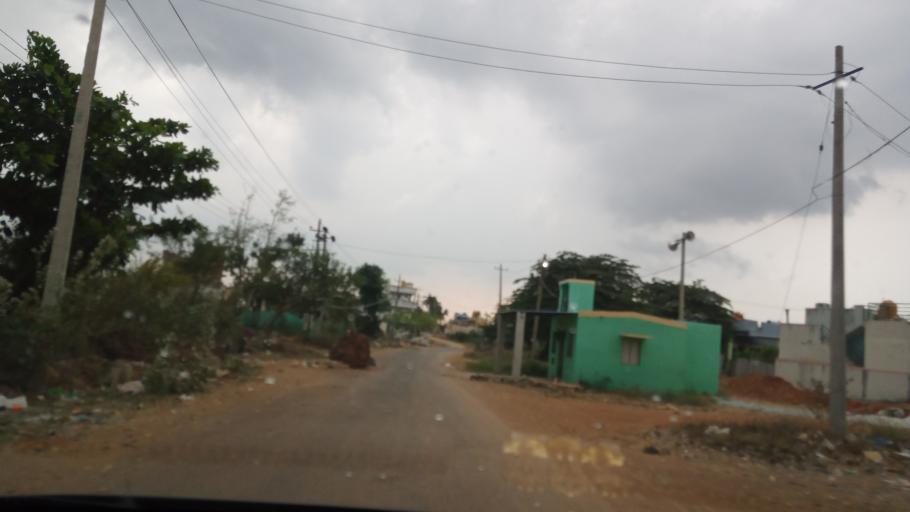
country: IN
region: Karnataka
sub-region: Kolar
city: Mulbagal
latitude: 13.1471
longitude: 78.3702
